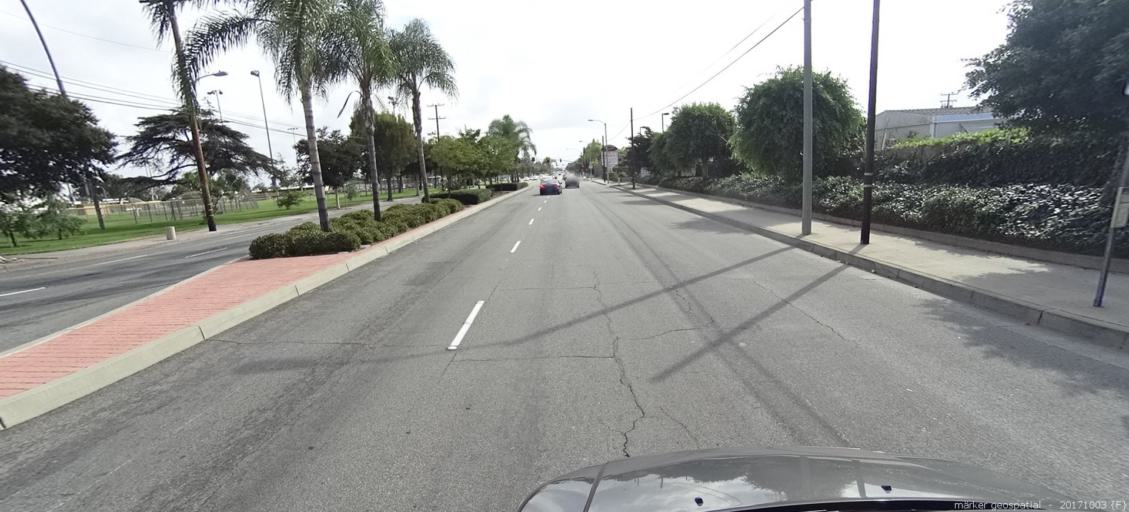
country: US
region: California
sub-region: Orange County
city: Midway City
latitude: 33.7594
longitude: -117.9678
